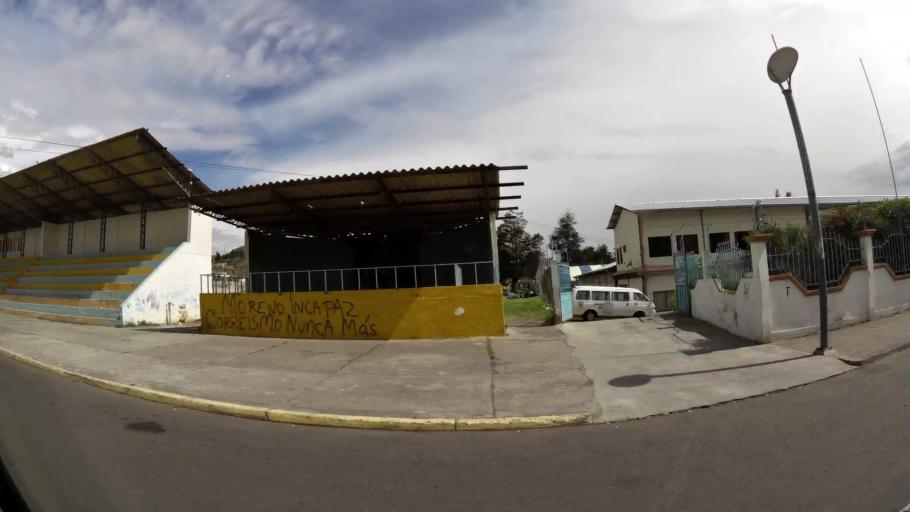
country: EC
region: Cotopaxi
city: Latacunga
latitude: -0.9360
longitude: -78.6074
